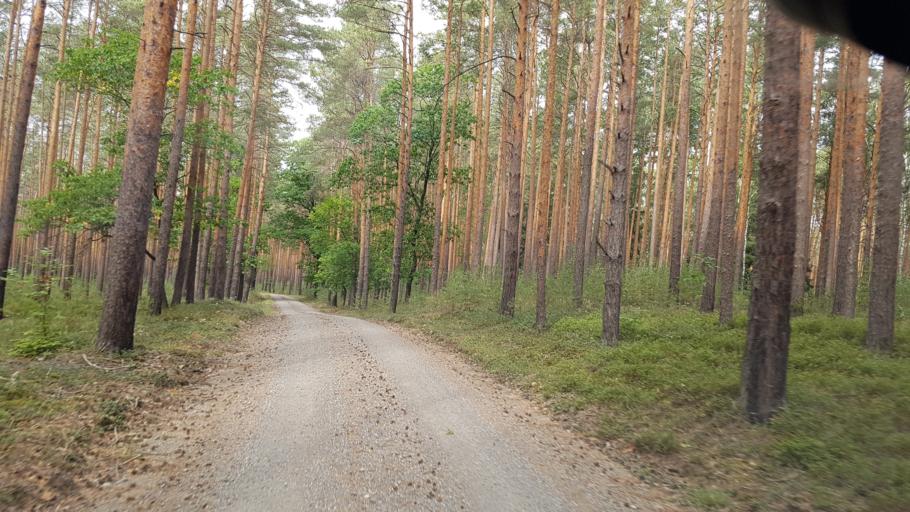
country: DE
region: Brandenburg
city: Ruckersdorf
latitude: 51.5734
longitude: 13.6150
